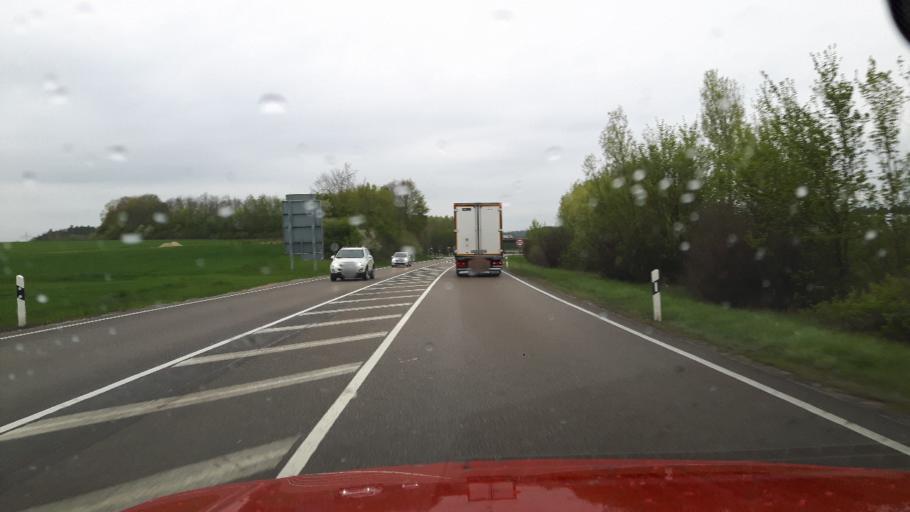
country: DE
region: Bavaria
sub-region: Regierungsbezirk Mittelfranken
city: Burgoberbach
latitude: 49.2537
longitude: 10.5909
